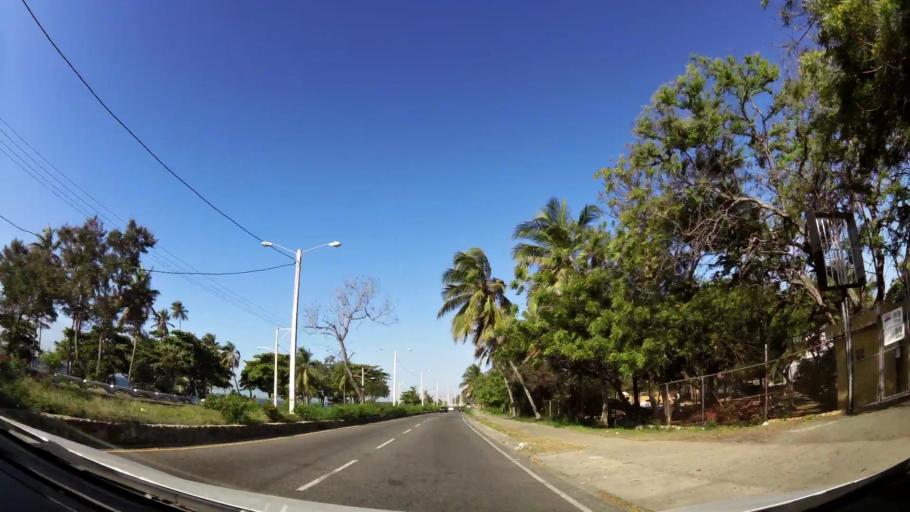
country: DO
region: Santo Domingo
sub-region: Santo Domingo
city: Santo Domingo Este
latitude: 18.4686
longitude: -69.8637
